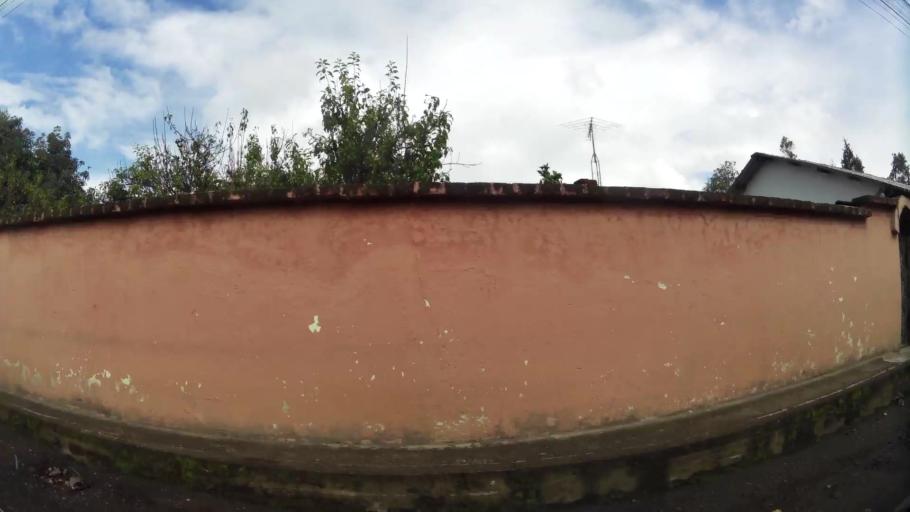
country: EC
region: Pichincha
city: Sangolqui
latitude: -0.3044
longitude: -78.4315
